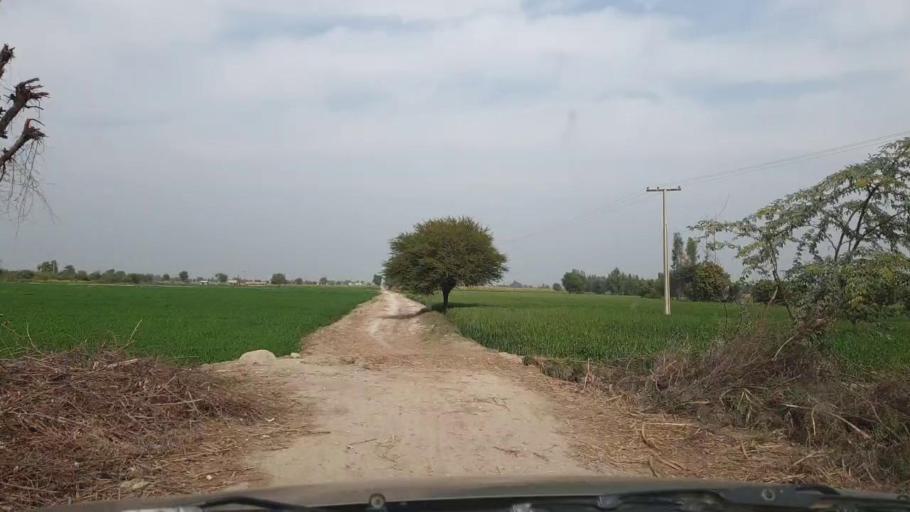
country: PK
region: Sindh
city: Sinjhoro
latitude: 26.0758
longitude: 68.8284
